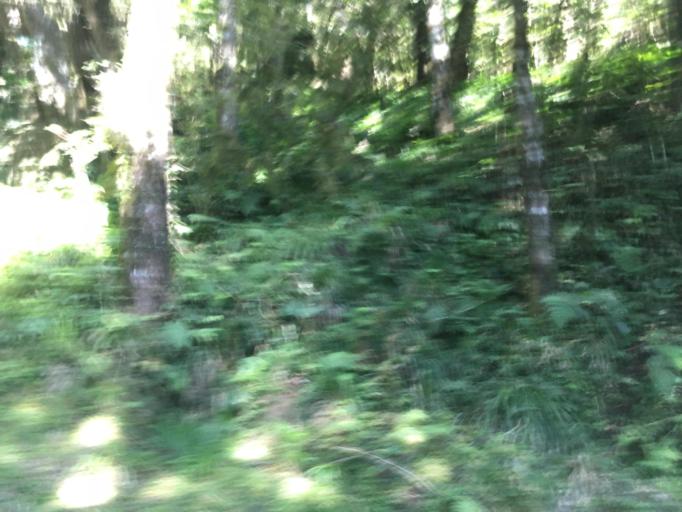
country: TW
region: Taiwan
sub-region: Yilan
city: Yilan
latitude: 24.6203
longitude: 121.4726
